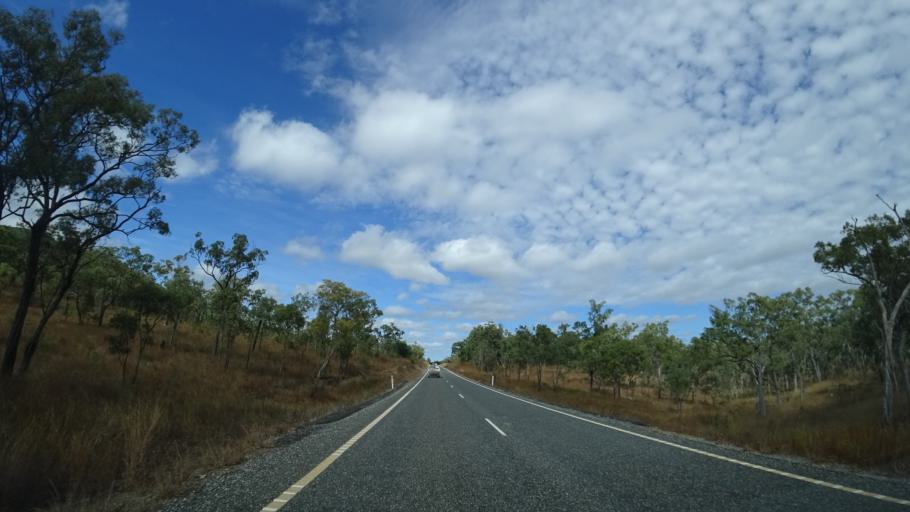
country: AU
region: Queensland
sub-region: Cairns
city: Port Douglas
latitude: -16.3447
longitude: 144.7262
